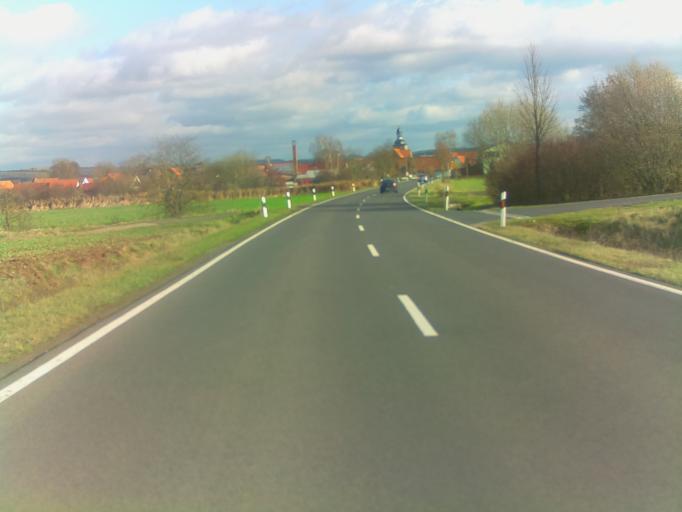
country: DE
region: Thuringia
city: Gleichamberg
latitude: 50.3607
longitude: 10.6280
